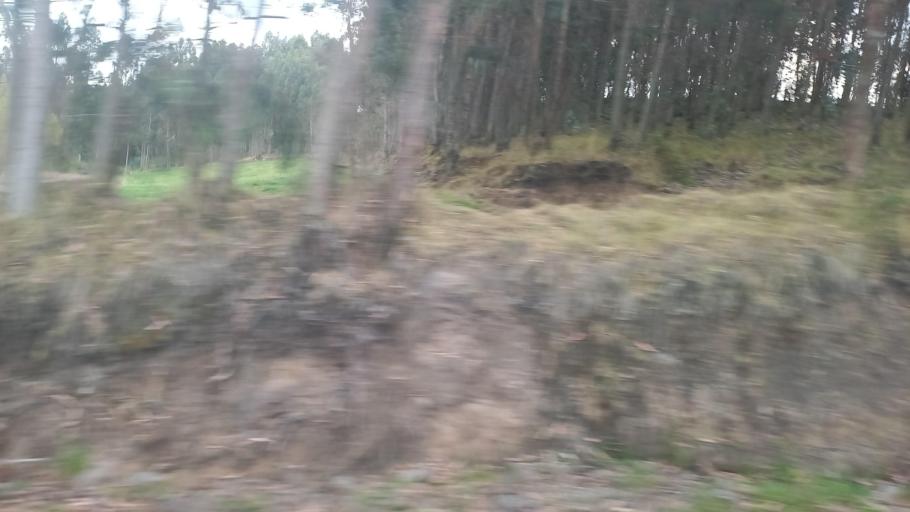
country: EC
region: Pichincha
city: Cayambe
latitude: 0.0738
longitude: -78.1086
